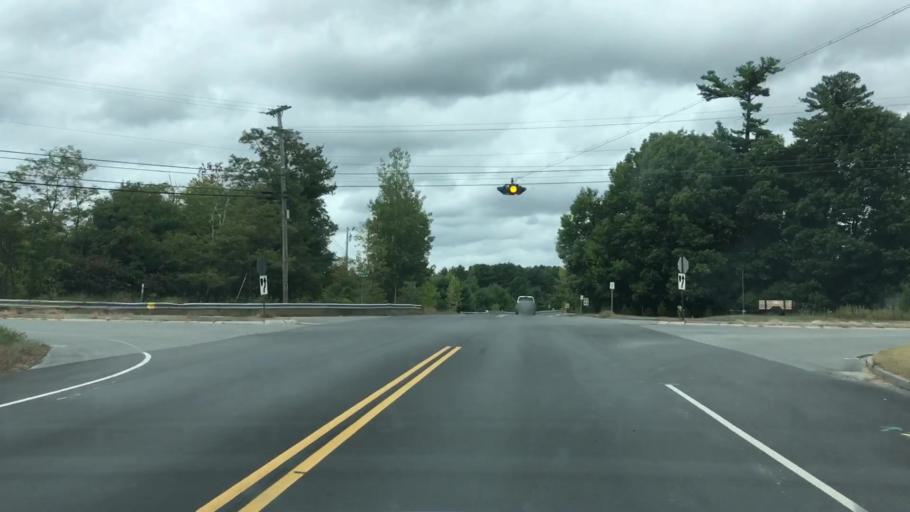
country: US
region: Maine
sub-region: Penobscot County
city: Milford
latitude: 44.9524
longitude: -68.6988
